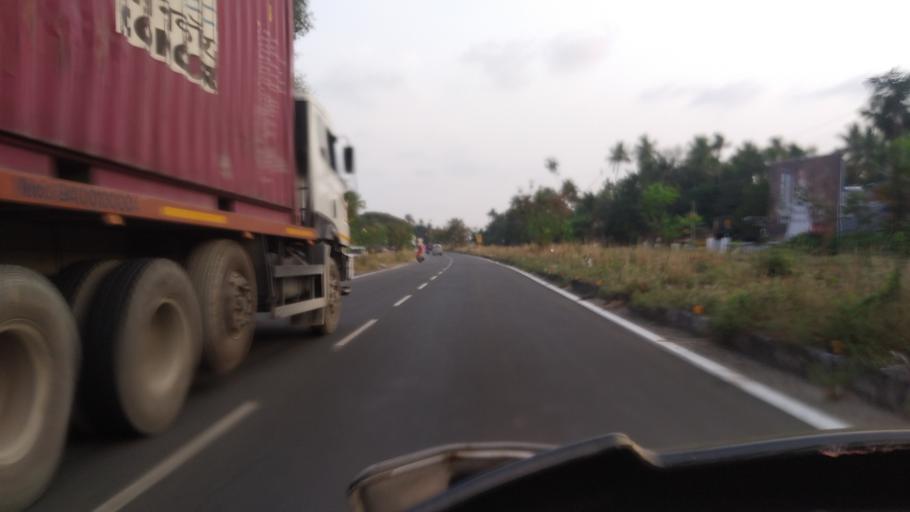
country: IN
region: Kerala
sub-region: Thrissur District
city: Kodungallur
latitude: 10.2290
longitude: 76.1955
